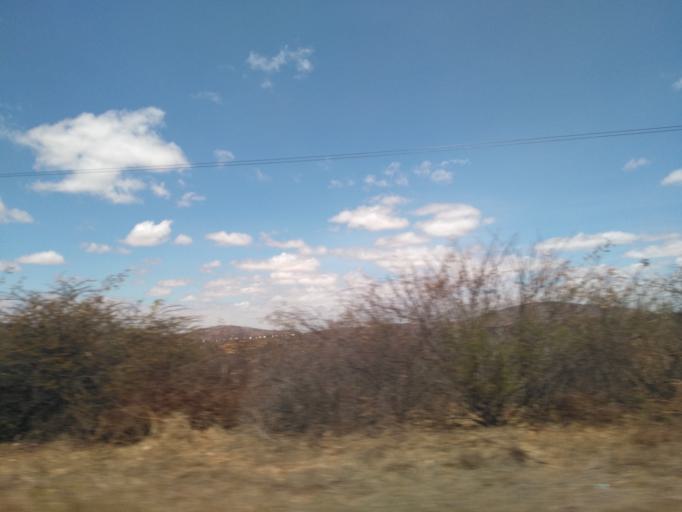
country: TZ
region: Dodoma
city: Kisasa
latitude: -6.2195
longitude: 35.8146
